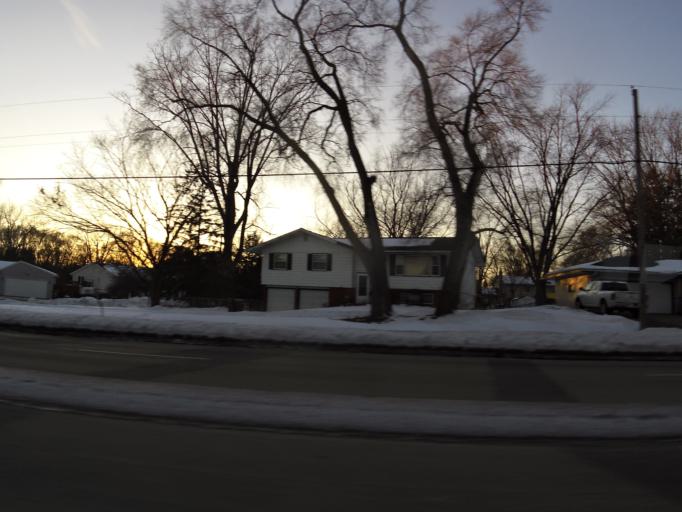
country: US
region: Minnesota
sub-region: Ramsey County
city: White Bear Lake
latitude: 45.0468
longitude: -93.0154
